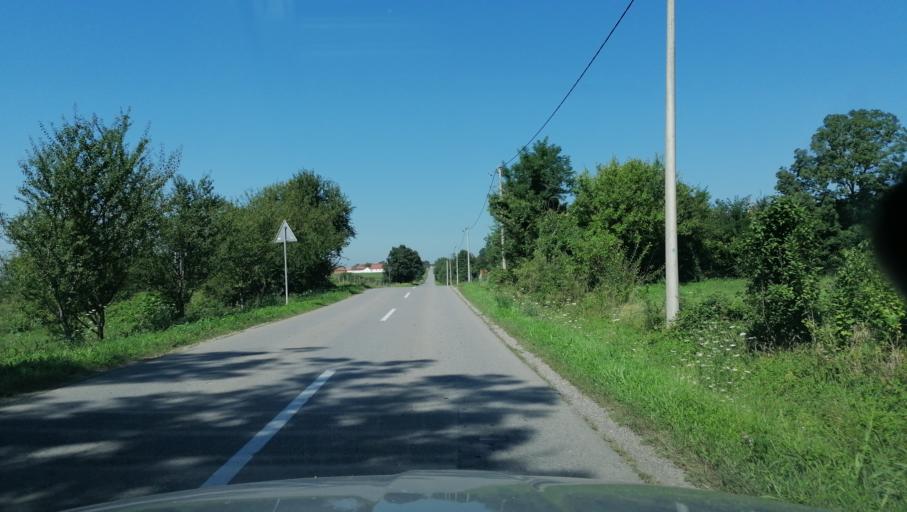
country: RS
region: Central Serbia
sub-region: Raski Okrug
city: Vrnjacka Banja
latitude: 43.6836
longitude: 20.8864
